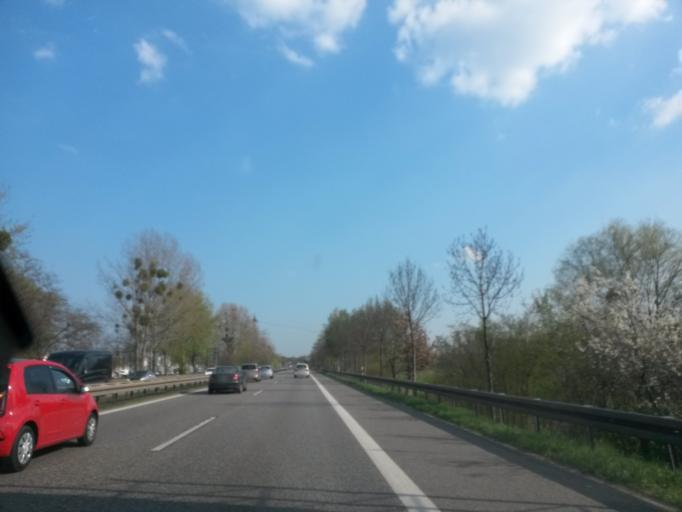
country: DE
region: Brandenburg
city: Potsdam
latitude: 52.3790
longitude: 13.1040
